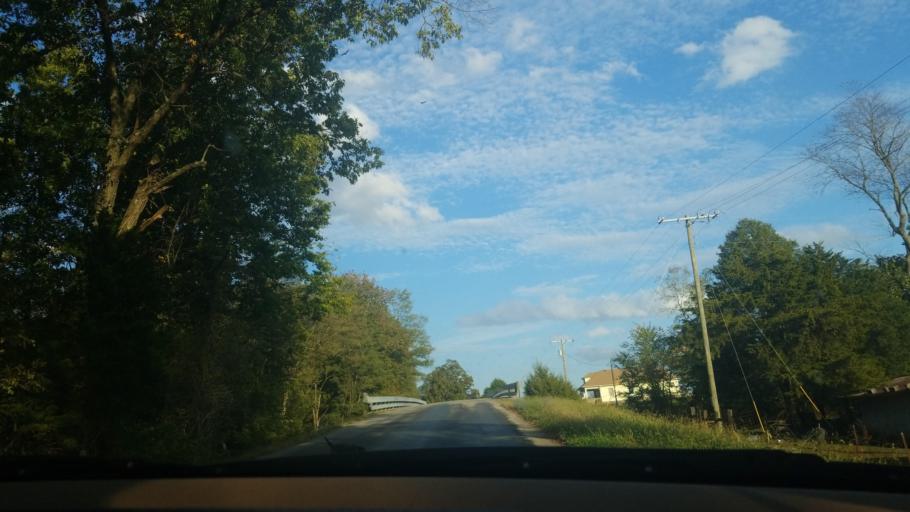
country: US
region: Illinois
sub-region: Saline County
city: Carrier Mills
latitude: 37.7721
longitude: -88.7154
